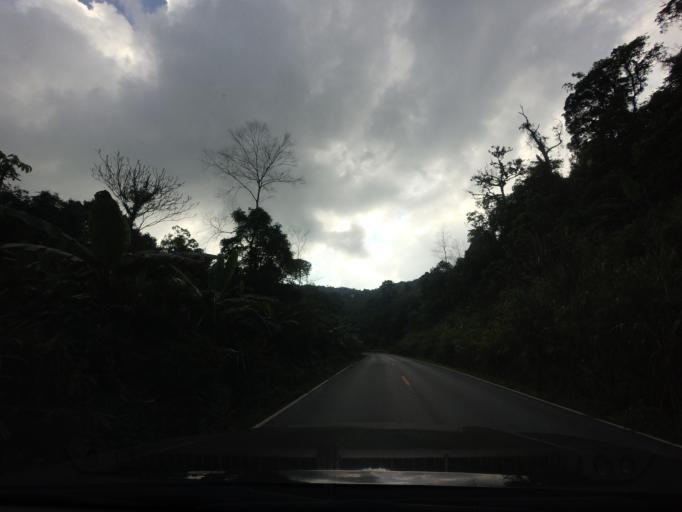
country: TH
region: Phetchabun
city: Lom Kao
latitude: 16.9423
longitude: 101.0411
